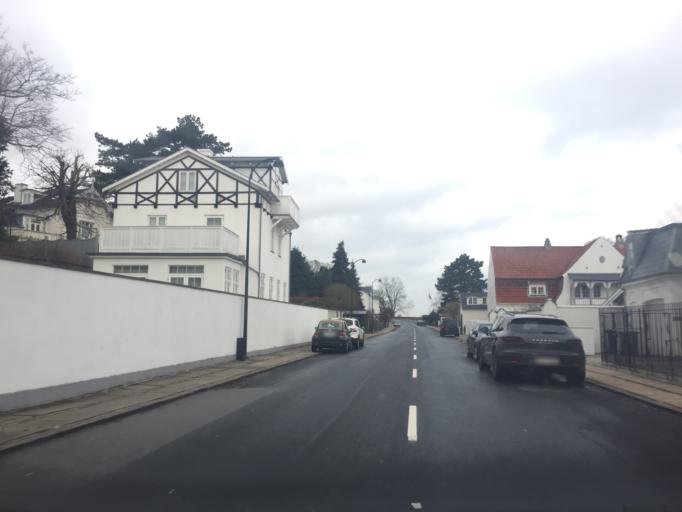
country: DK
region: Capital Region
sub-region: Gentofte Kommune
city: Charlottenlund
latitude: 55.7692
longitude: 12.5951
